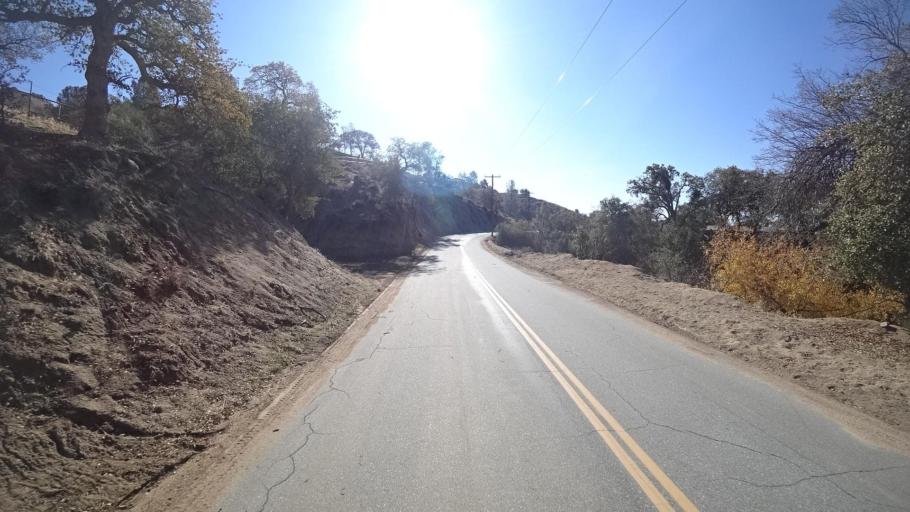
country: US
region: California
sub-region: Kern County
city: Bodfish
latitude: 35.3740
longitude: -118.3999
